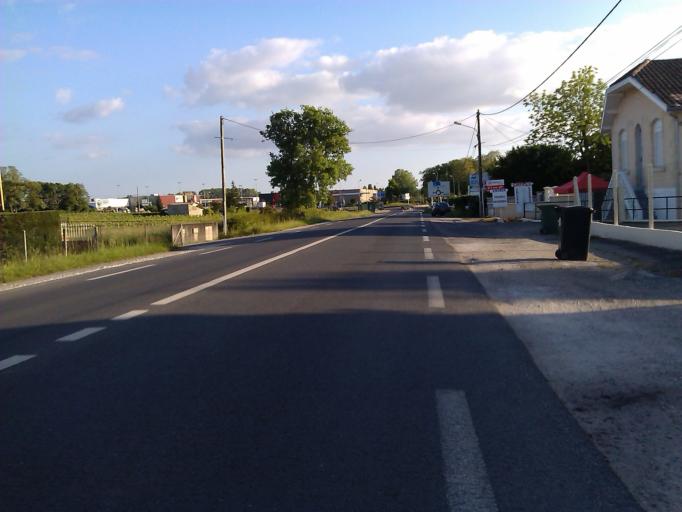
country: FR
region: Aquitaine
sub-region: Departement de la Gironde
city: Ambares-et-Lagrave
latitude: 44.9209
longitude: -0.4794
